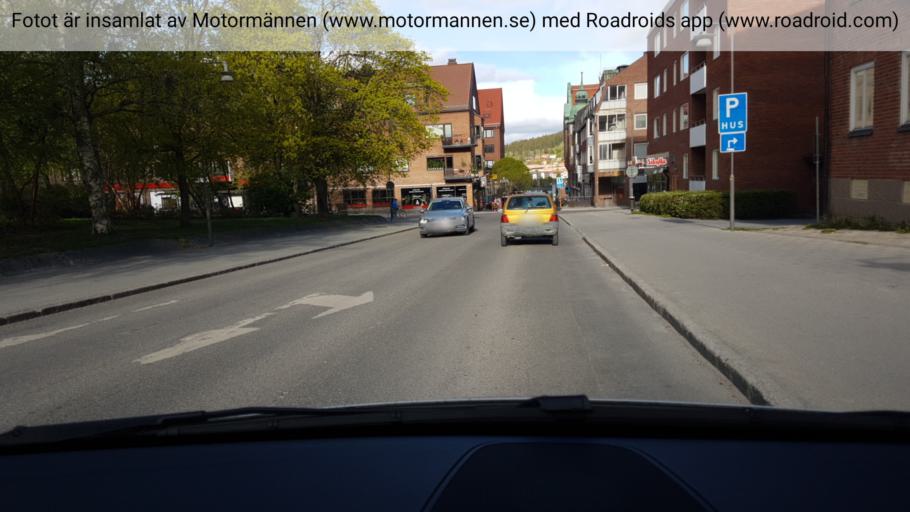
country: SE
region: Jaemtland
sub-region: OEstersunds Kommun
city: Ostersund
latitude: 63.1791
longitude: 14.6392
